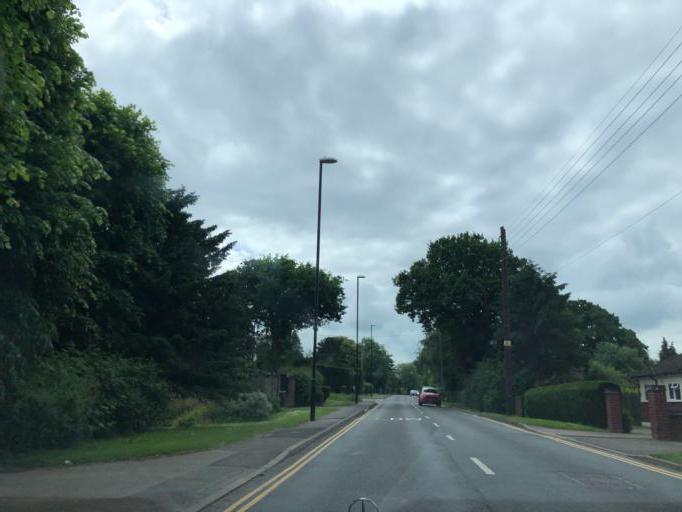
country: GB
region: England
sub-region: Warwickshire
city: Kenilworth
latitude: 52.3932
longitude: -1.5972
